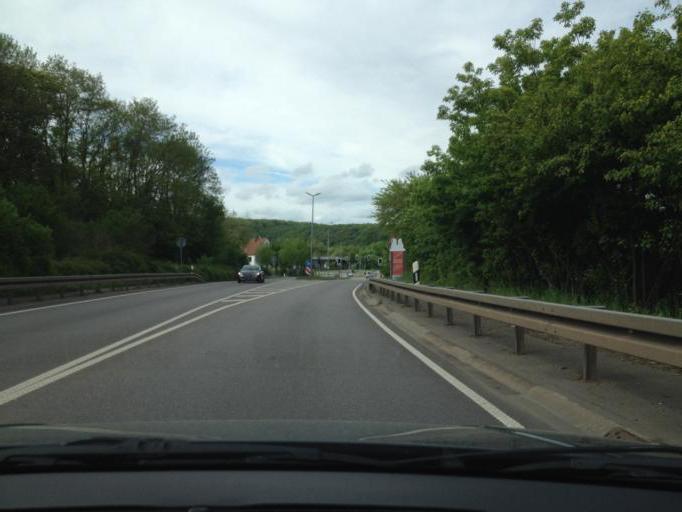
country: DE
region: Saarland
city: Bexbach
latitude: 49.3468
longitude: 7.2229
